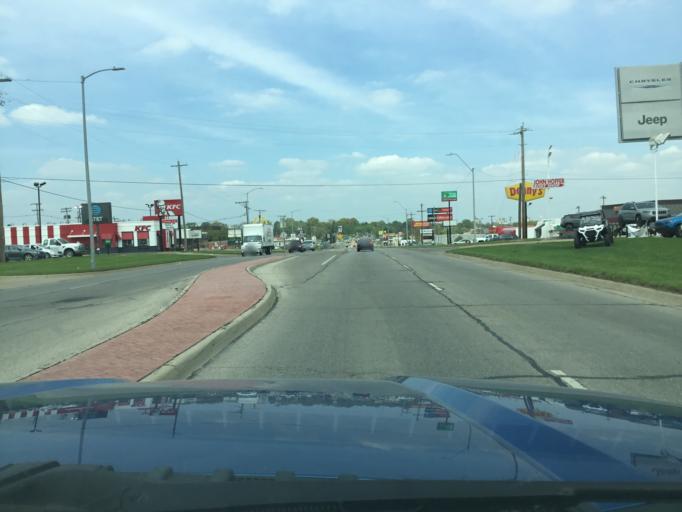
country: US
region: Kansas
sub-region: Shawnee County
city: Topeka
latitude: 39.0094
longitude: -95.6876
